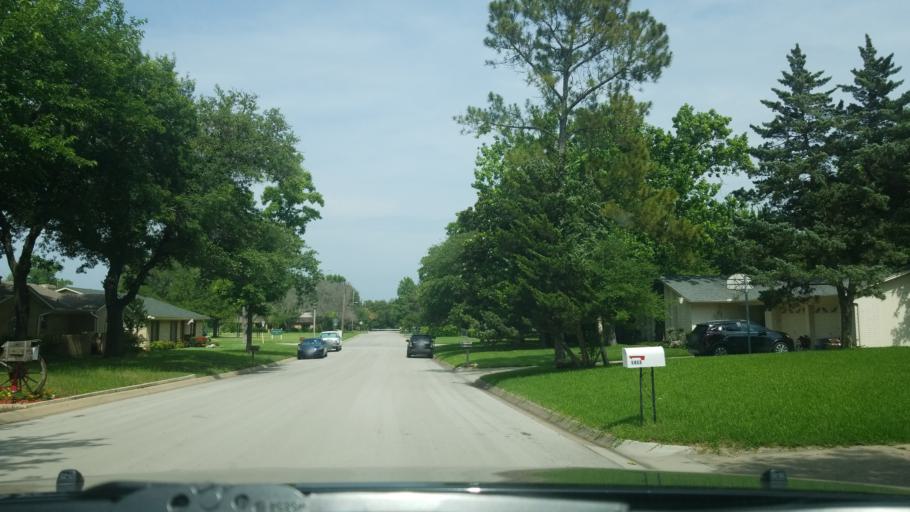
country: US
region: Texas
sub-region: Denton County
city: Denton
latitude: 33.2362
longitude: -97.1503
